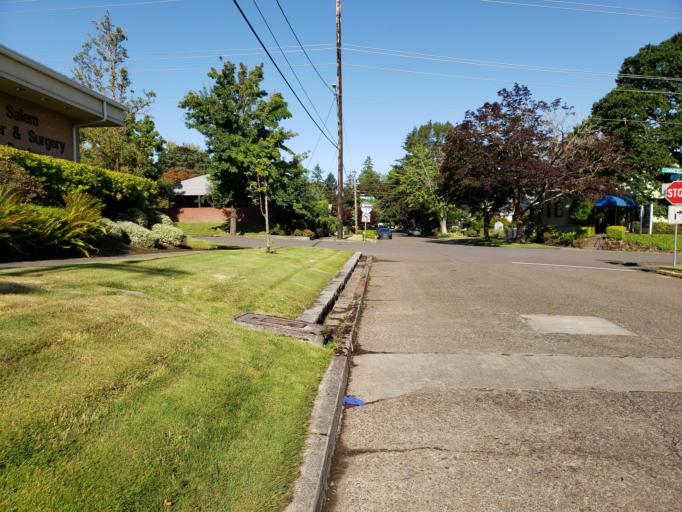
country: US
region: Oregon
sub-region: Marion County
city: Salem
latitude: 44.9282
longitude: -123.0439
